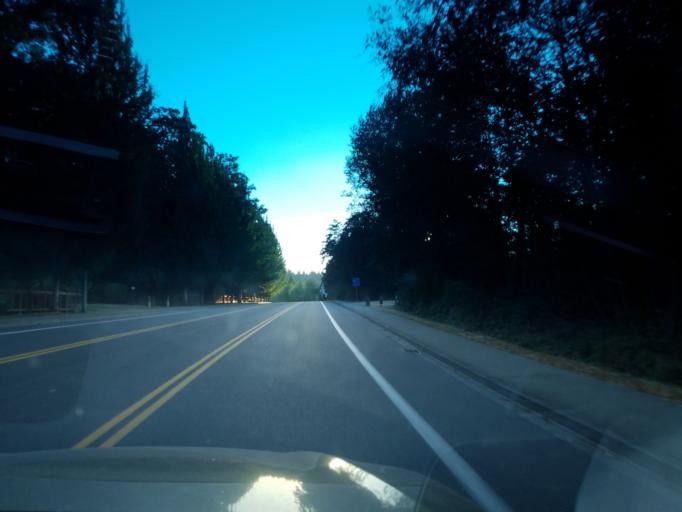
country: US
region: Washington
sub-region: King County
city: City of Sammamish
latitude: 47.6015
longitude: -122.0169
